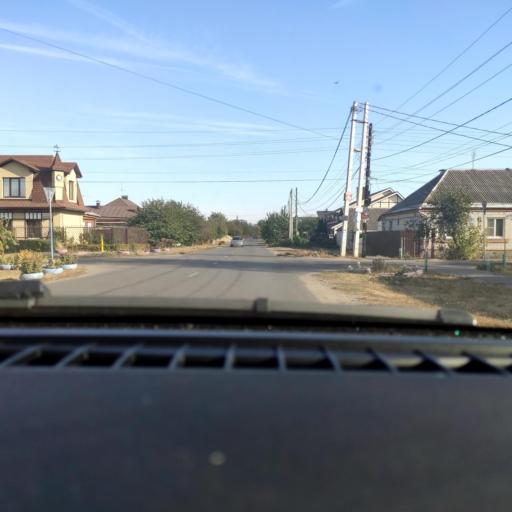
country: RU
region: Voronezj
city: Voronezh
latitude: 51.6666
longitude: 39.2570
